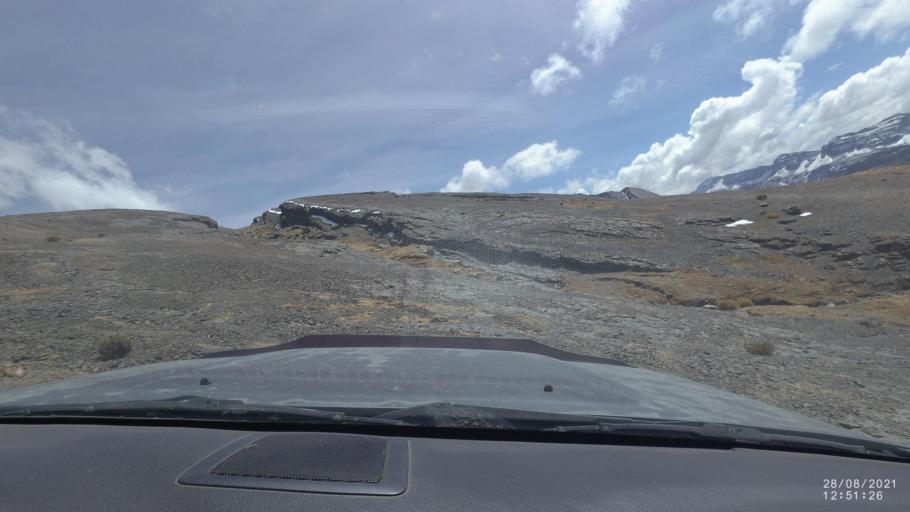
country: BO
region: Cochabamba
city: Sipe Sipe
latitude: -17.2821
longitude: -66.3833
